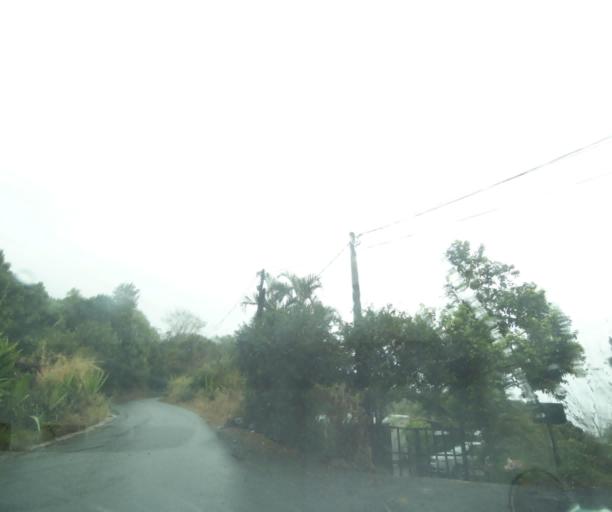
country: RE
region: Reunion
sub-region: Reunion
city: La Possession
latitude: -20.9817
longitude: 55.3410
